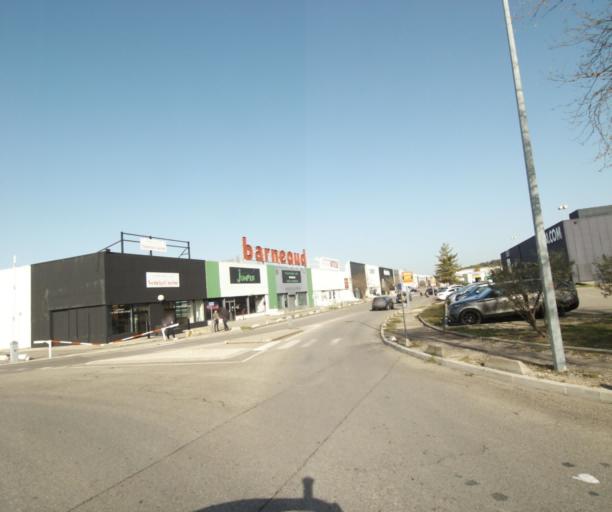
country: FR
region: Provence-Alpes-Cote d'Azur
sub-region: Departement des Bouches-du-Rhone
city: Septemes-les-Vallons
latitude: 43.4158
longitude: 5.3595
